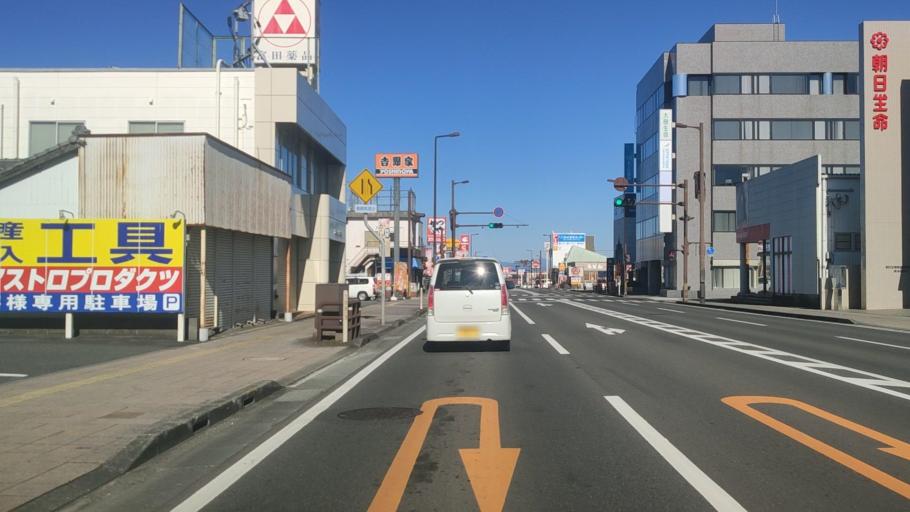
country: JP
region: Miyazaki
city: Miyakonojo
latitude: 31.7332
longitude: 131.0685
